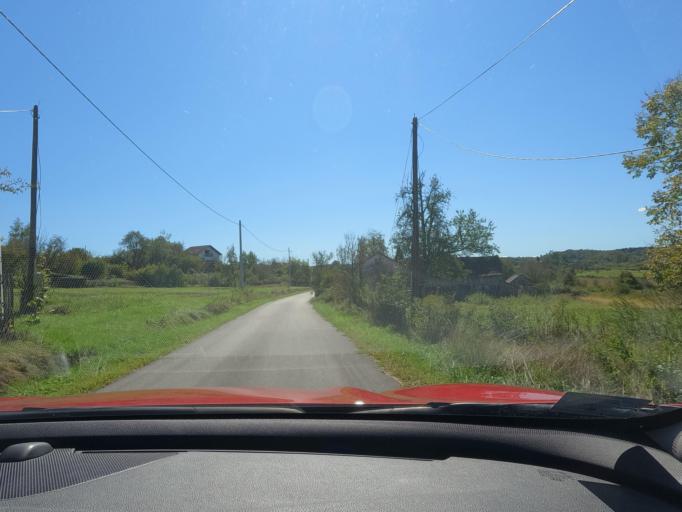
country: HR
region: Sisacko-Moslavacka
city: Petrinja
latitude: 45.3522
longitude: 16.2497
